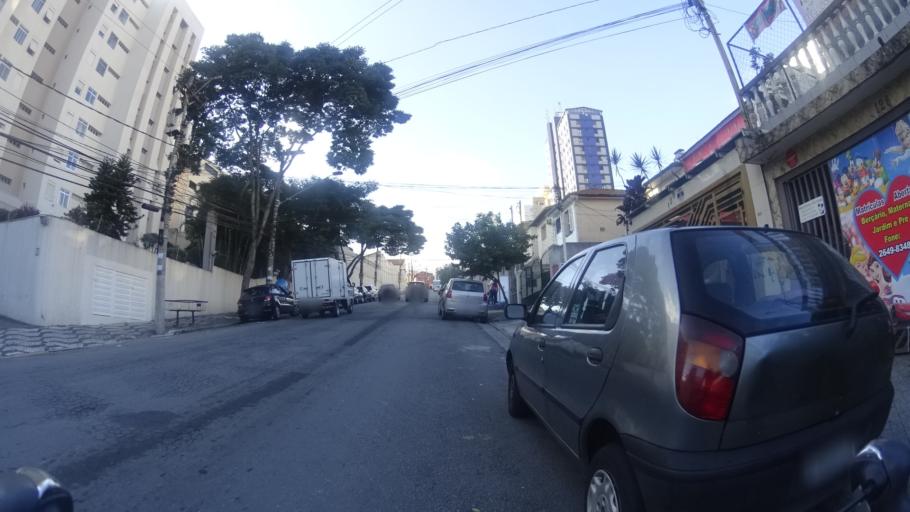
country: BR
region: Sao Paulo
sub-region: Sao Paulo
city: Sao Paulo
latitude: -23.5017
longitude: -46.6316
